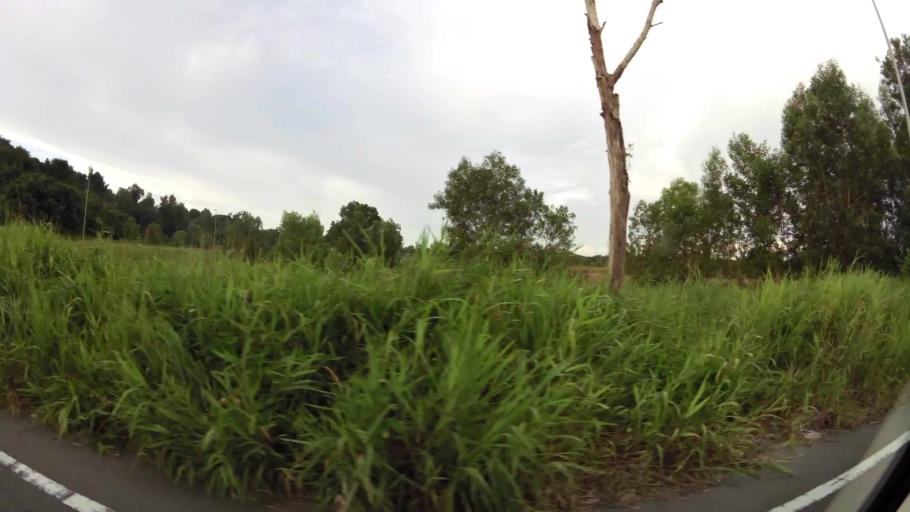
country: BN
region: Brunei and Muara
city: Bandar Seri Begawan
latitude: 4.9989
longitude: 114.9897
